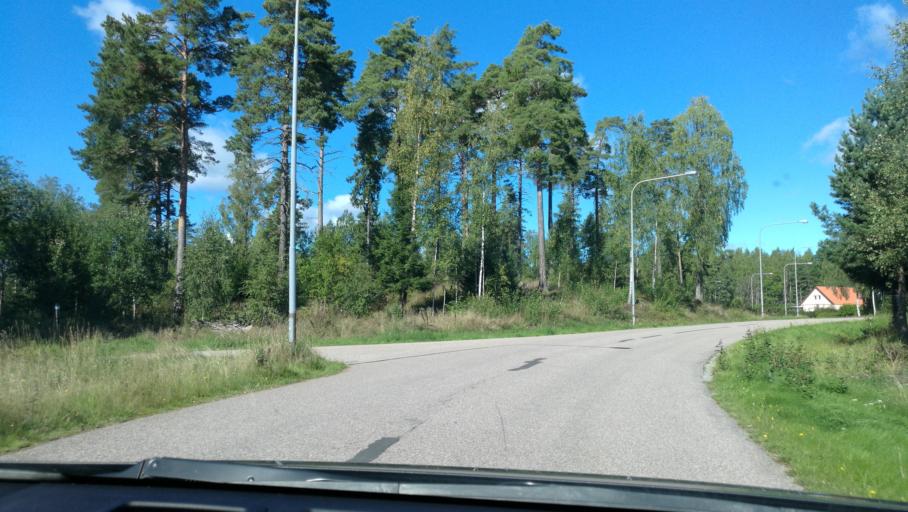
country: SE
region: Vaestmanland
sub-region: Surahammars Kommun
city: Surahammar
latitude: 59.6910
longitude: 16.2363
